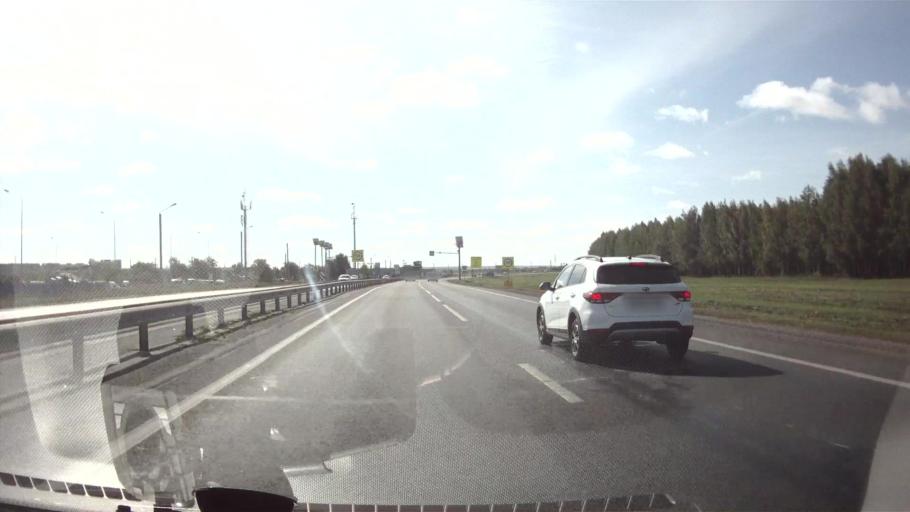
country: RU
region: Ulyanovsk
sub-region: Ulyanovskiy Rayon
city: Ulyanovsk
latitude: 54.2771
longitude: 48.2604
